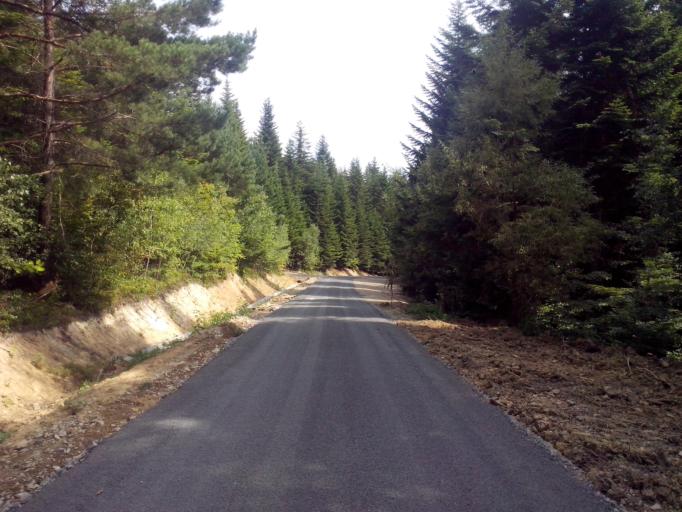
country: PL
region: Subcarpathian Voivodeship
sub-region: Powiat strzyzowski
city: Strzyzow
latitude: 49.8117
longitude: 21.7998
